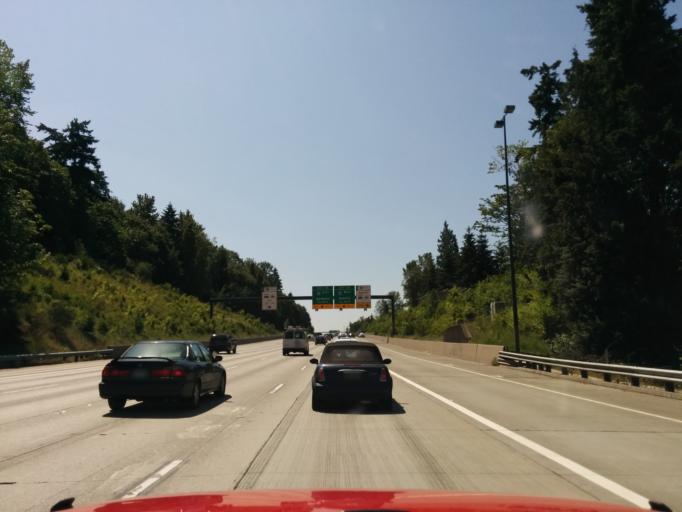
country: US
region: Washington
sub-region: King County
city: Bellevue
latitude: 47.5972
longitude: -122.1817
